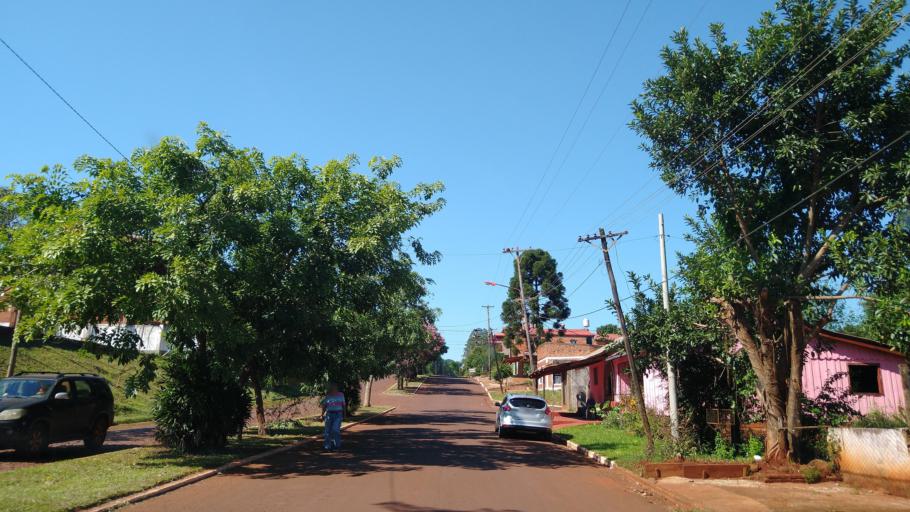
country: AR
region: Misiones
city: Puerto Esperanza
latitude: -26.0299
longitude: -54.6121
